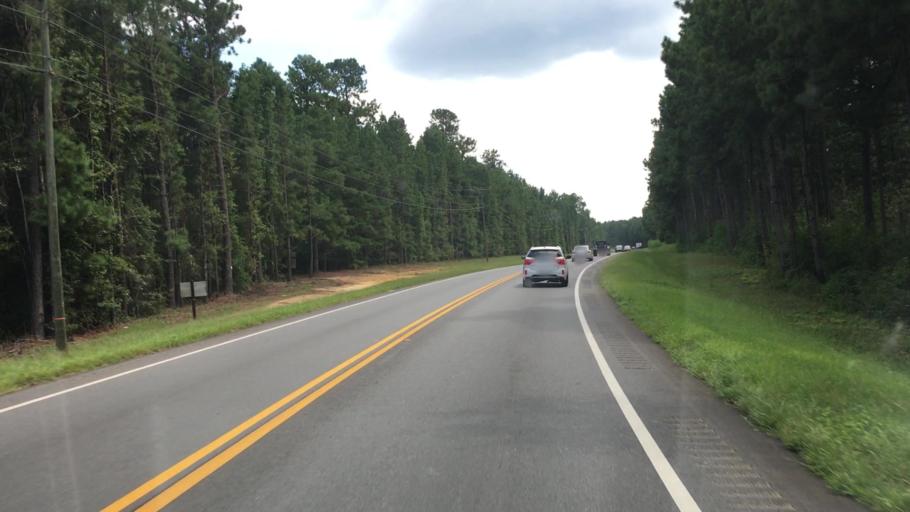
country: US
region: Georgia
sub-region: Putnam County
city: Jefferson
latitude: 33.4049
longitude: -83.3677
